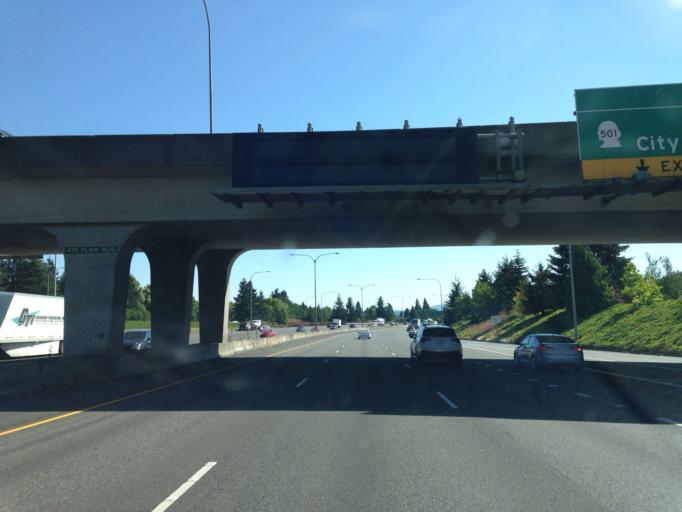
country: US
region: Washington
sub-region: Clark County
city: Vancouver
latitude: 45.6390
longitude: -122.6620
